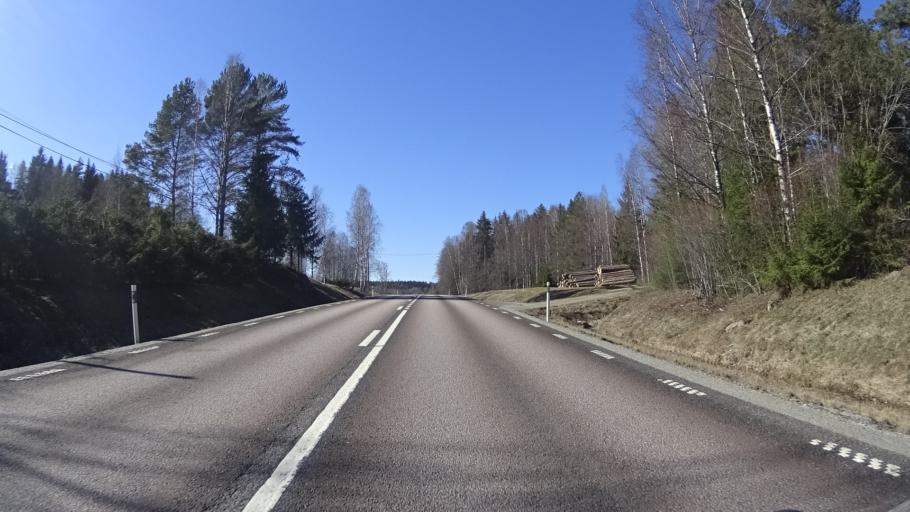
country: SE
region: Vaermland
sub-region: Sunne Kommun
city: Sunne
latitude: 59.6642
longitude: 12.9185
